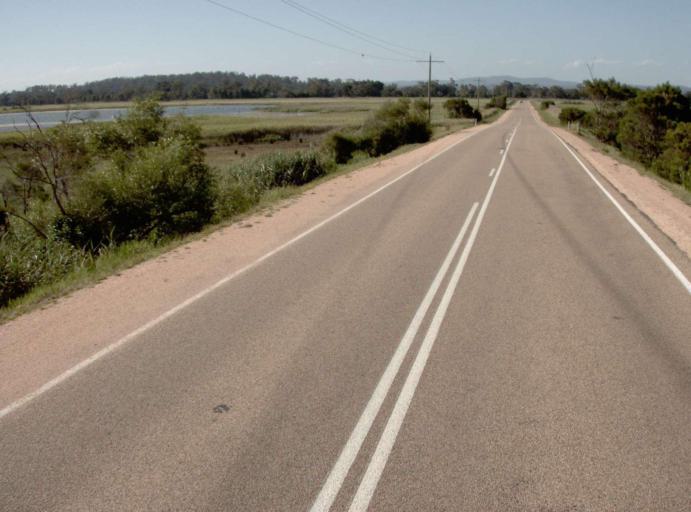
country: AU
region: Victoria
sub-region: East Gippsland
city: Lakes Entrance
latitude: -37.7783
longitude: 148.5388
